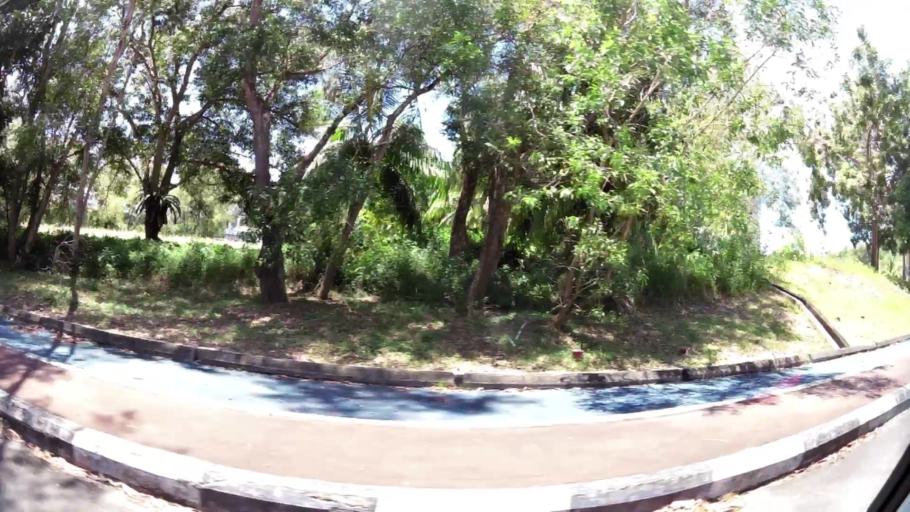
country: BN
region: Brunei and Muara
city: Bandar Seri Begawan
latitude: 4.9177
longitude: 114.9430
